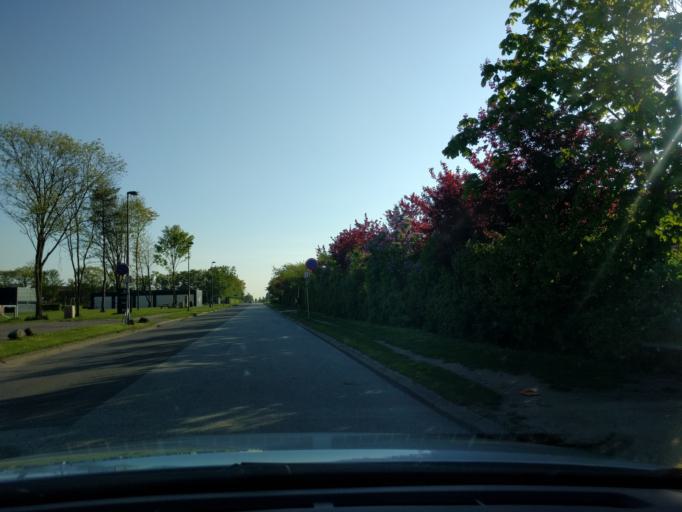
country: DK
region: Zealand
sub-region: Guldborgsund Kommune
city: Nykobing Falster
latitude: 54.7773
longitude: 11.8782
